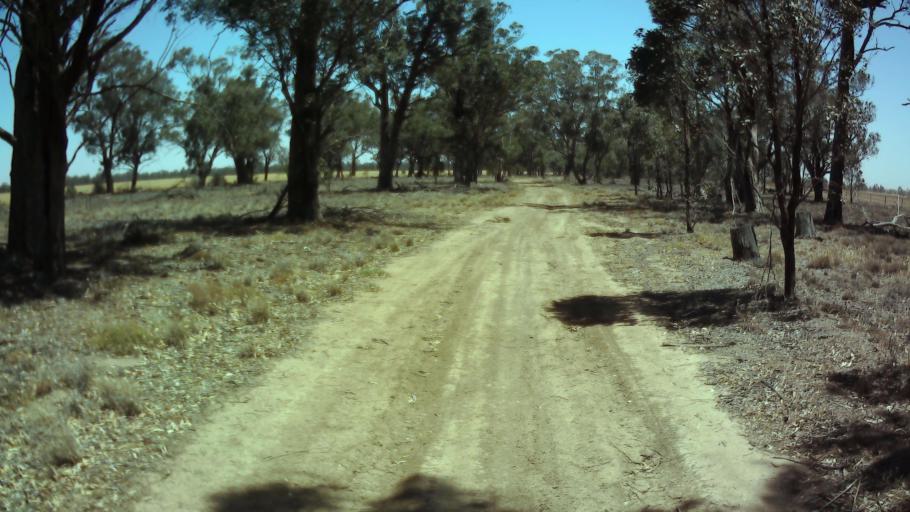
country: AU
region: New South Wales
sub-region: Weddin
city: Grenfell
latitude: -34.0547
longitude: 147.8231
